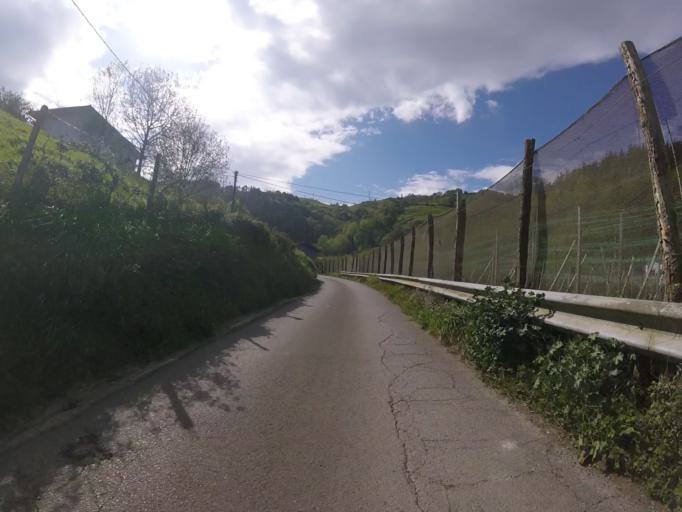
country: ES
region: Basque Country
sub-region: Provincia de Guipuzcoa
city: Aizarnazabal
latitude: 43.2522
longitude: -2.2346
